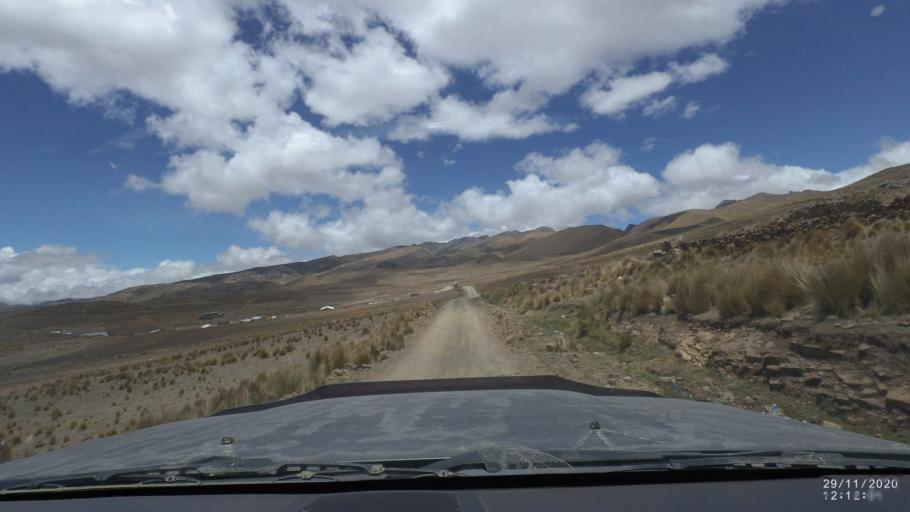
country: BO
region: Cochabamba
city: Cochabamba
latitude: -17.1154
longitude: -66.3035
